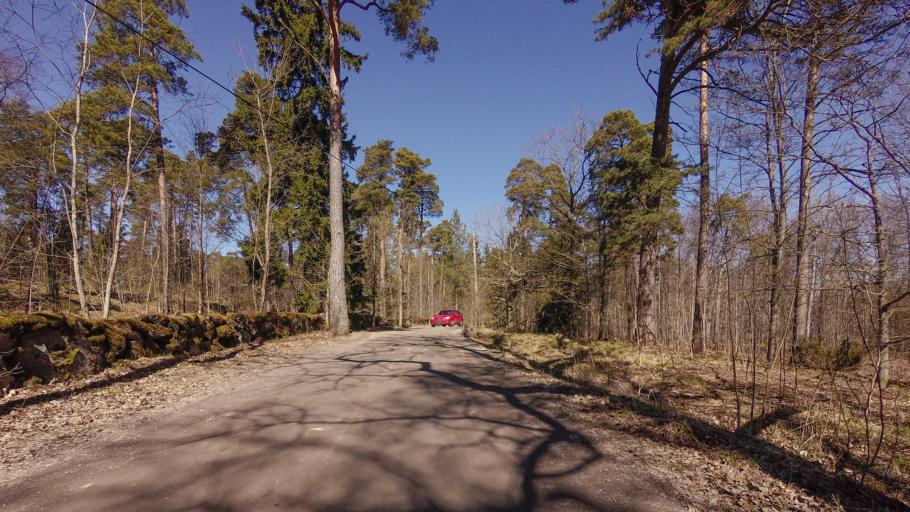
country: FI
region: Uusimaa
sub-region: Helsinki
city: Helsinki
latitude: 60.1659
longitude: 25.0272
